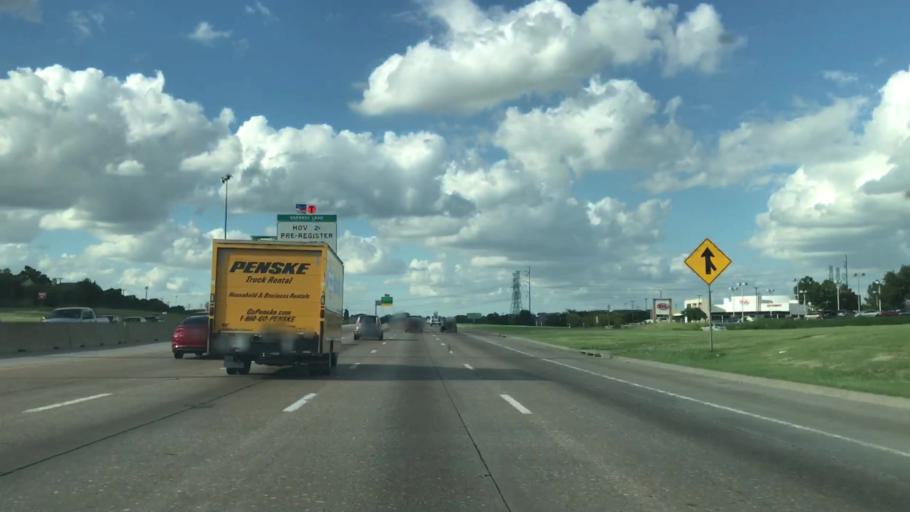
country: US
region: Texas
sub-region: Dallas County
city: Mesquite
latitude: 32.8359
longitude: -96.6323
